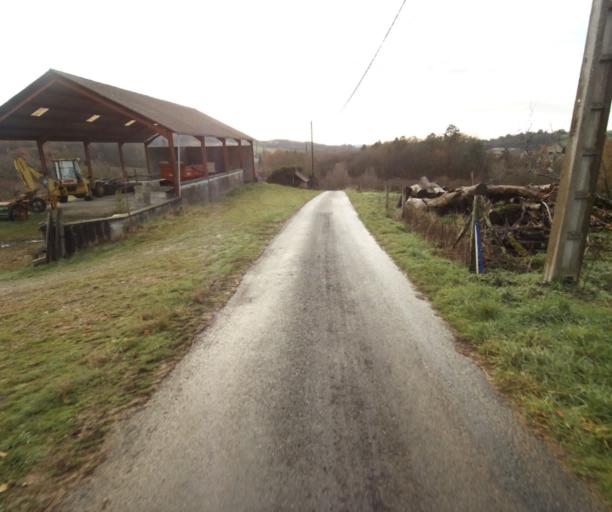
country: FR
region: Limousin
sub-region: Departement de la Correze
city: Saint-Mexant
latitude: 45.2519
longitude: 1.6393
